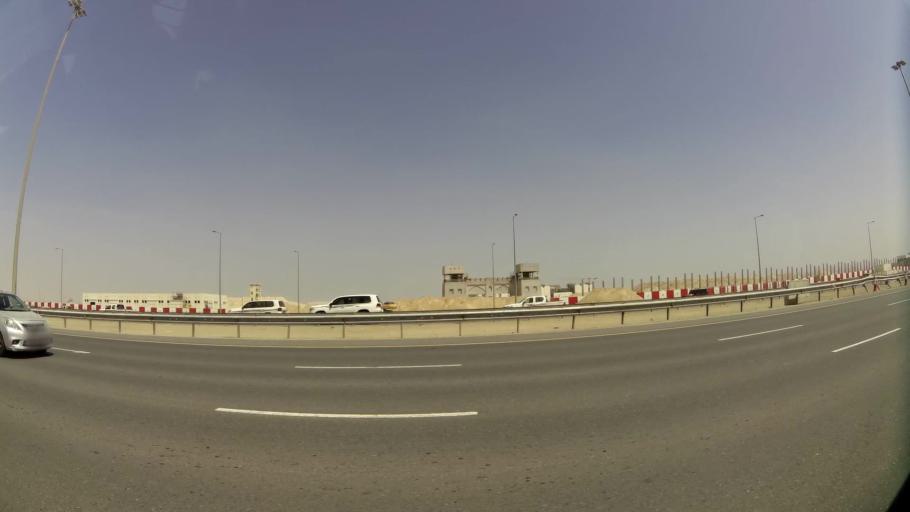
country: QA
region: Baladiyat ar Rayyan
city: Ar Rayyan
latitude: 25.3597
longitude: 51.4503
